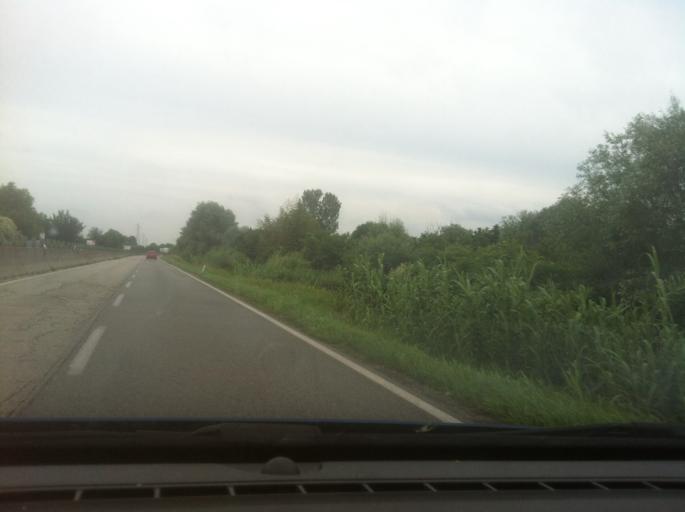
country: IT
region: Piedmont
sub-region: Provincia di Torino
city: Settimo Torinese
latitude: 45.1277
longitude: 7.7726
